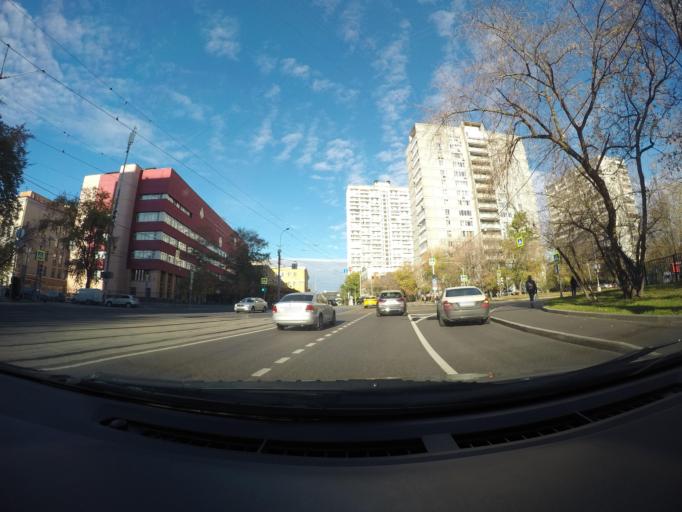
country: RU
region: Moscow
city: Rostokino
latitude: 55.8252
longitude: 37.6521
